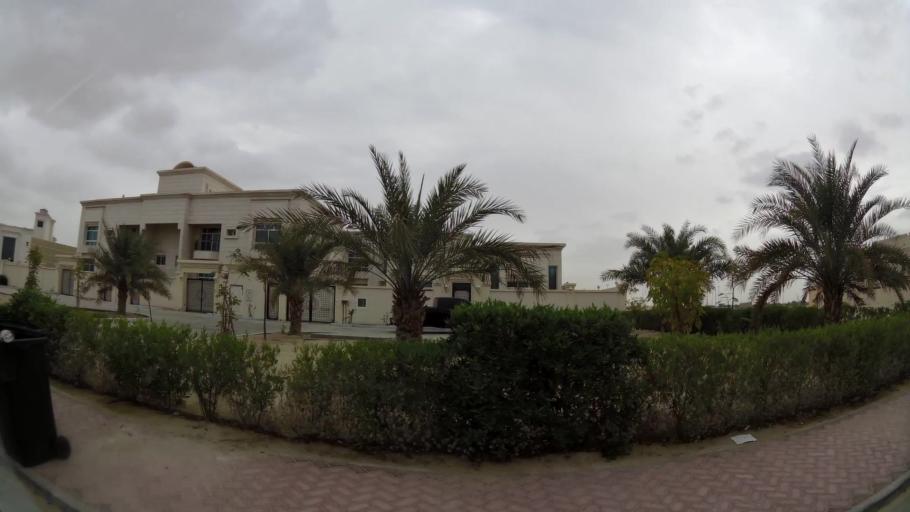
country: AE
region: Abu Dhabi
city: Abu Dhabi
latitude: 24.3747
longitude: 54.6508
